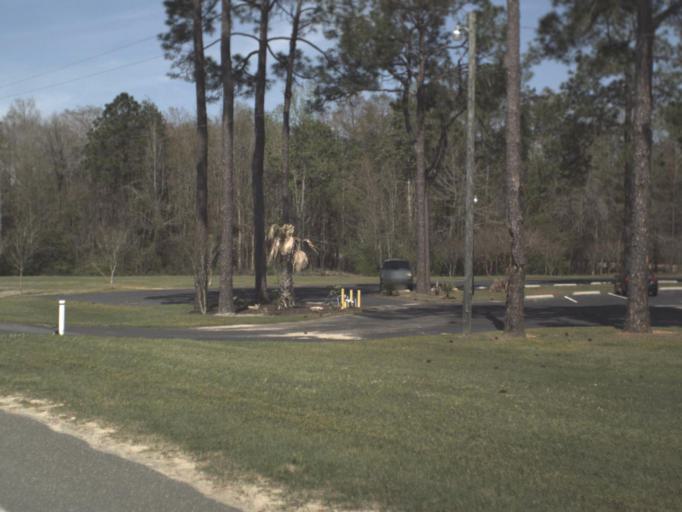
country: US
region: Florida
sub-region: Holmes County
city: Bonifay
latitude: 30.7870
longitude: -85.6592
